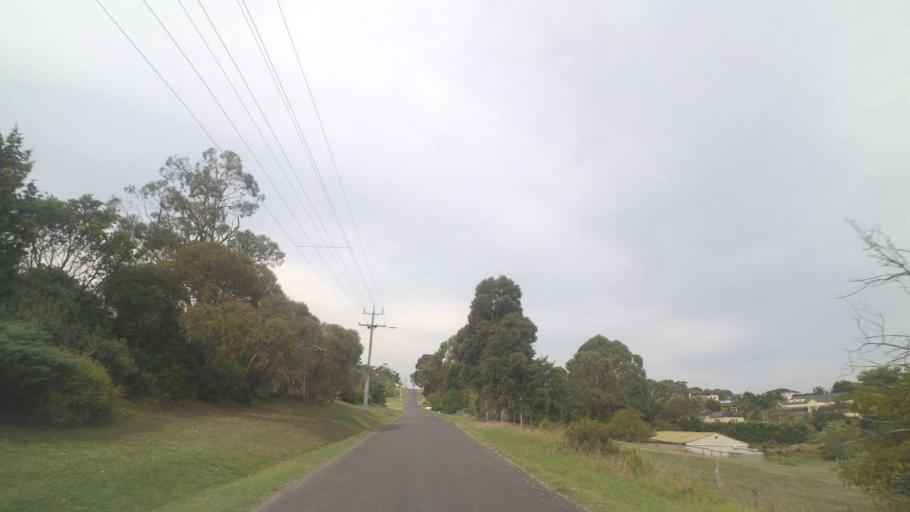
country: AU
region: Victoria
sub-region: Manningham
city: Park Orchards
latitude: -37.7608
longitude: 145.1927
